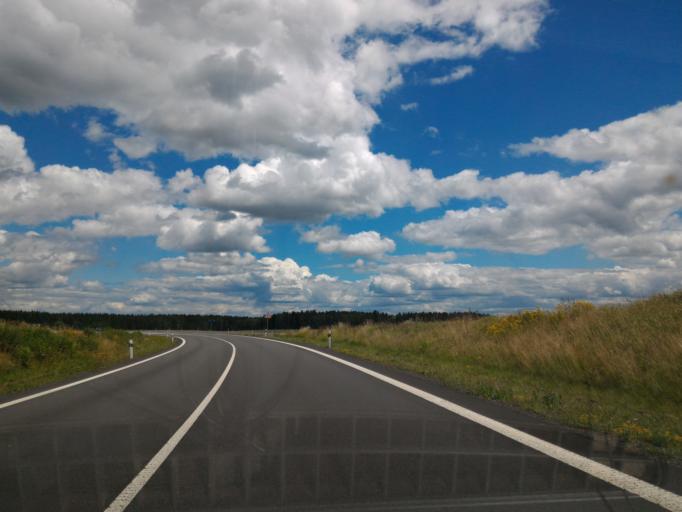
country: CZ
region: Vysocina
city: Bohdalov
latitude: 49.4846
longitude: 15.8803
